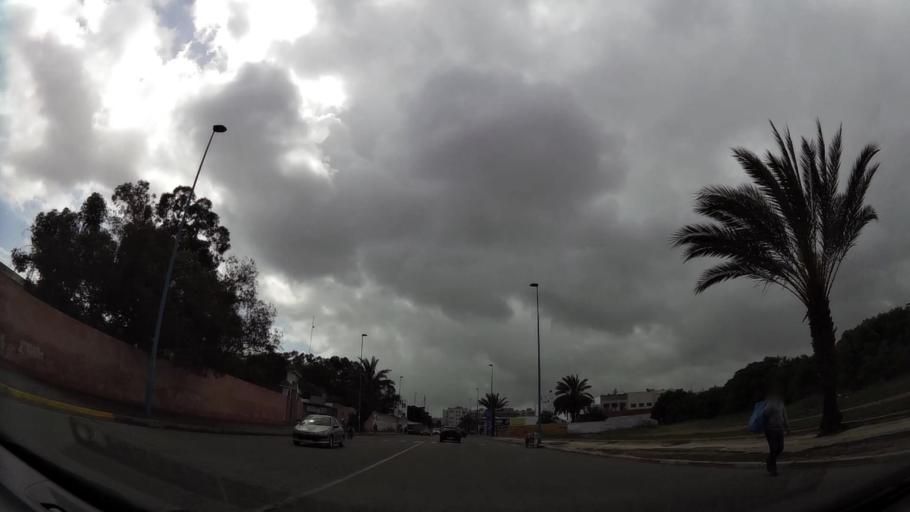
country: MA
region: Grand Casablanca
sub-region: Casablanca
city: Casablanca
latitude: 33.5429
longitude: -7.6017
